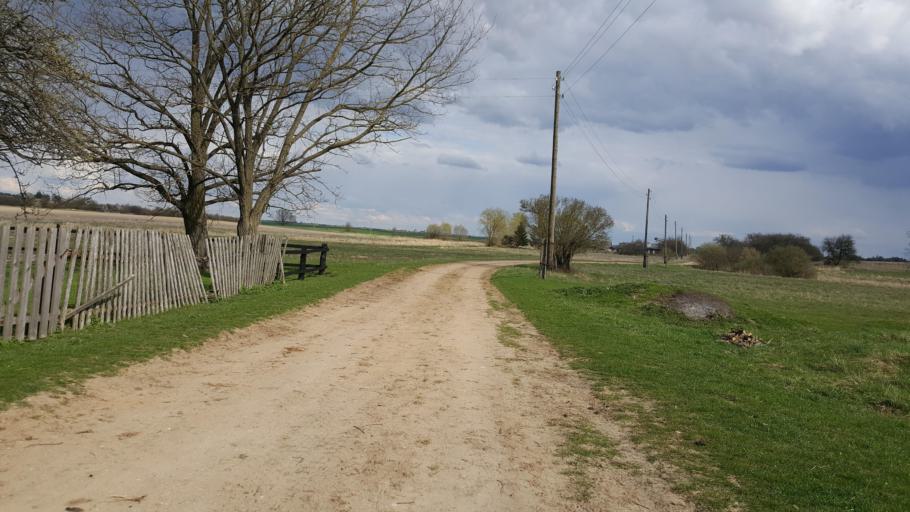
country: BY
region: Brest
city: Kamyanyets
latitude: 52.4367
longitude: 23.6843
